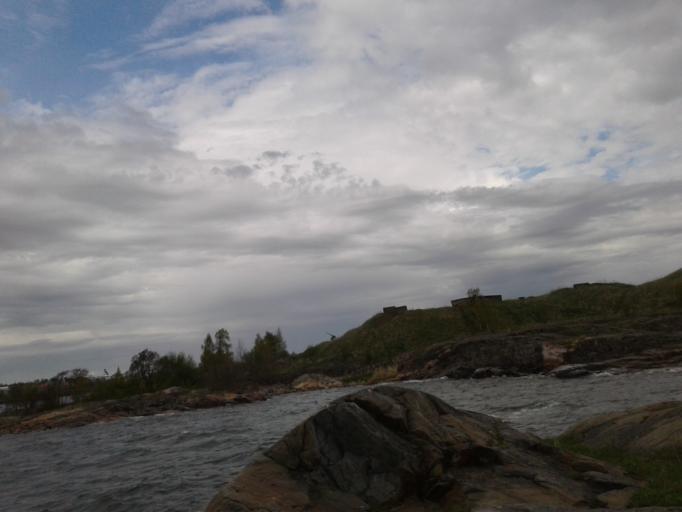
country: FI
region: Uusimaa
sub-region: Helsinki
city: Helsinki
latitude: 60.1466
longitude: 24.9735
